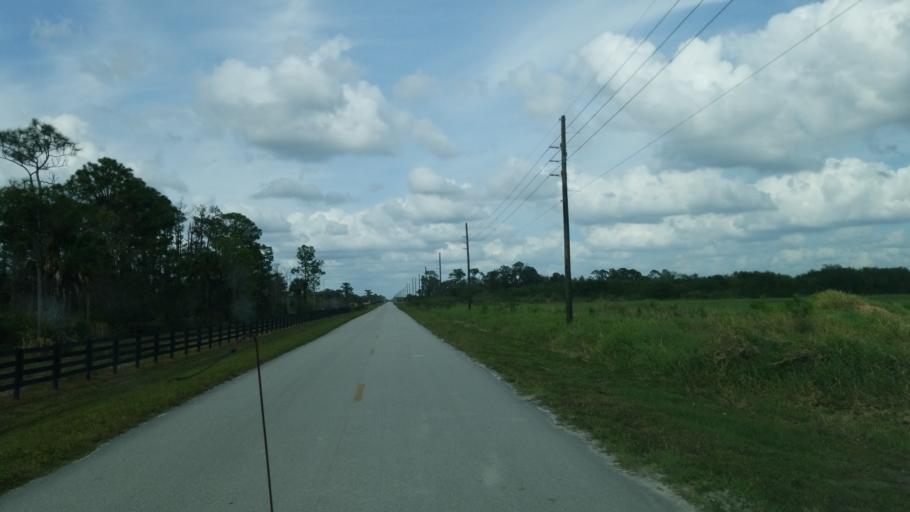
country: US
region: Florida
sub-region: Okeechobee County
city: Cypress Quarters
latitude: 27.4815
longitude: -80.7724
